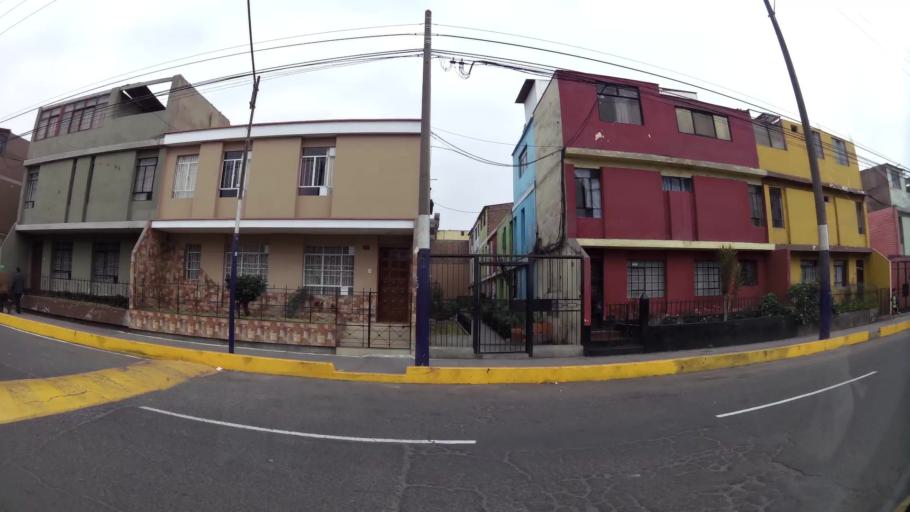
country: PE
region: Lima
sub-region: Lima
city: Surco
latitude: -12.1725
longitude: -77.0197
